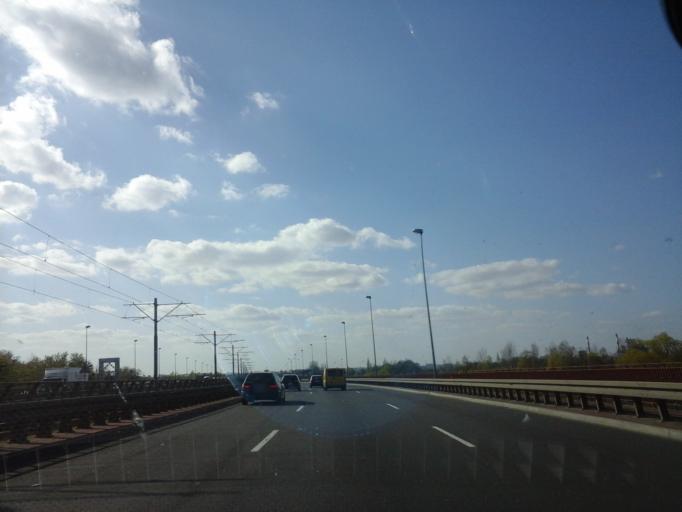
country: PL
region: West Pomeranian Voivodeship
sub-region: Szczecin
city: Szczecin
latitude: 53.3952
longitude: 14.6093
